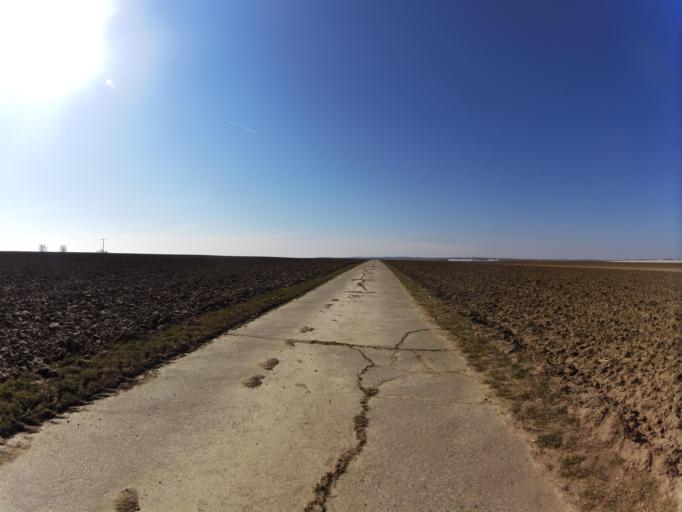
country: DE
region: Bavaria
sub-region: Regierungsbezirk Unterfranken
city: Oberpleichfeld
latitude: 49.8822
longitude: 10.0815
